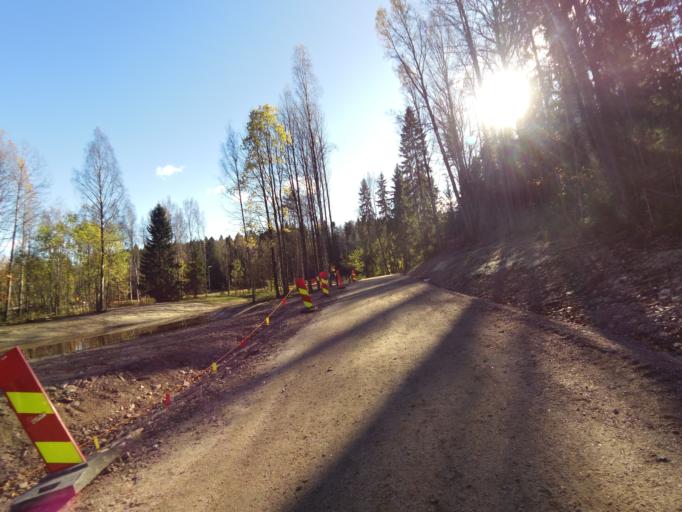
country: FI
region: Uusimaa
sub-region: Helsinki
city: Kauniainen
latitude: 60.1774
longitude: 24.7130
